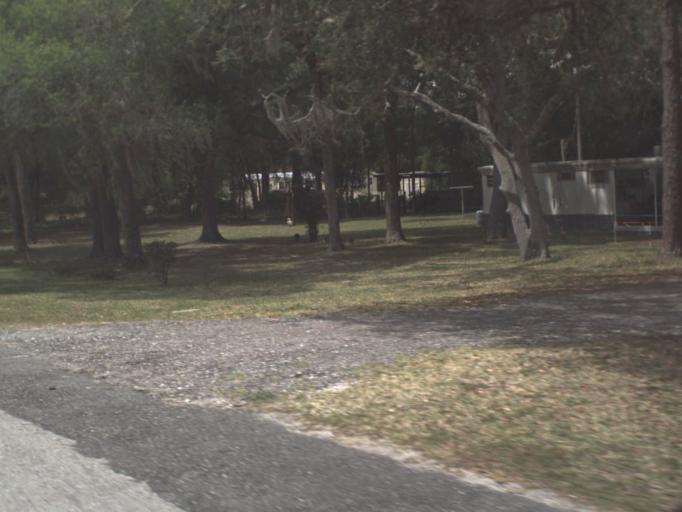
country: US
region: Florida
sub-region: Lake County
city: Lake Mack-Forest Hills
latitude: 28.8971
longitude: -81.4576
